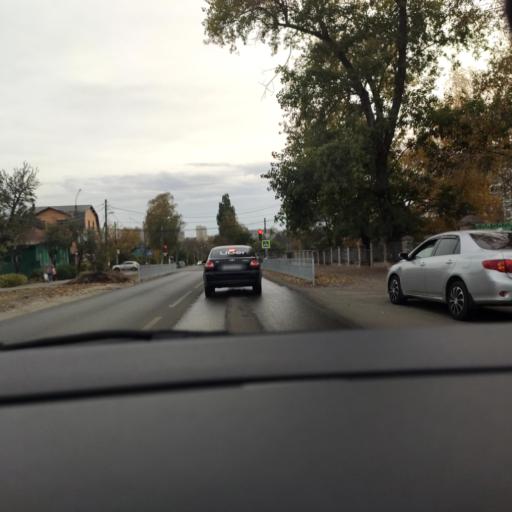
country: RU
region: Voronezj
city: Voronezh
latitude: 51.6963
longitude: 39.1897
